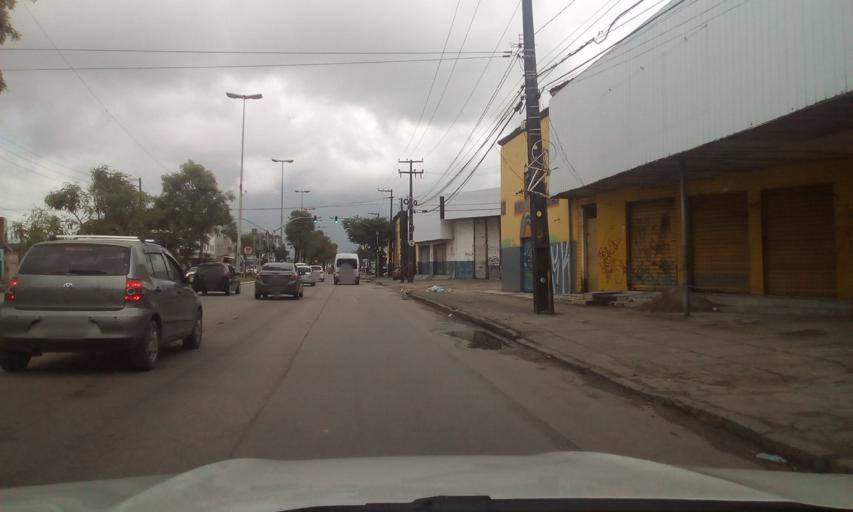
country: BR
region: Pernambuco
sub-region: Recife
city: Recife
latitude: -8.0637
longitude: -34.9351
